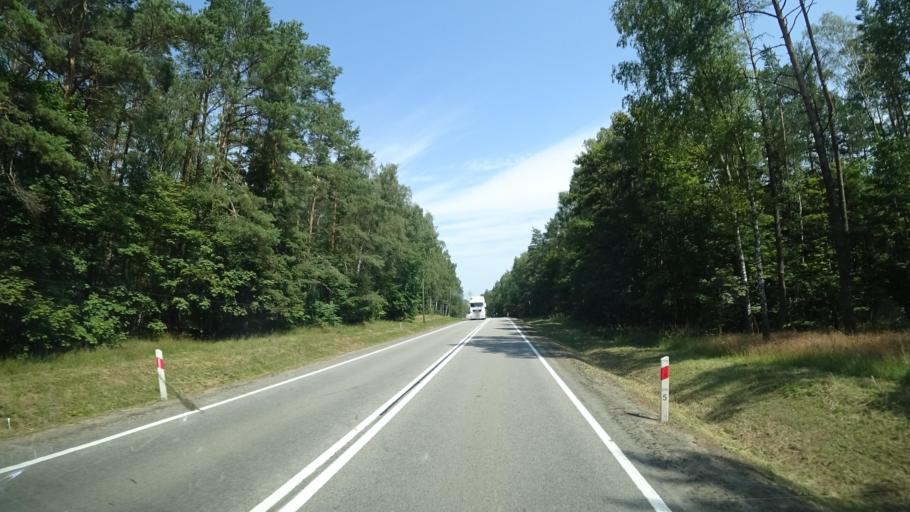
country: PL
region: Pomeranian Voivodeship
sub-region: Powiat koscierski
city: Grabowo Koscierskie
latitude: 54.1811
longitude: 18.0908
